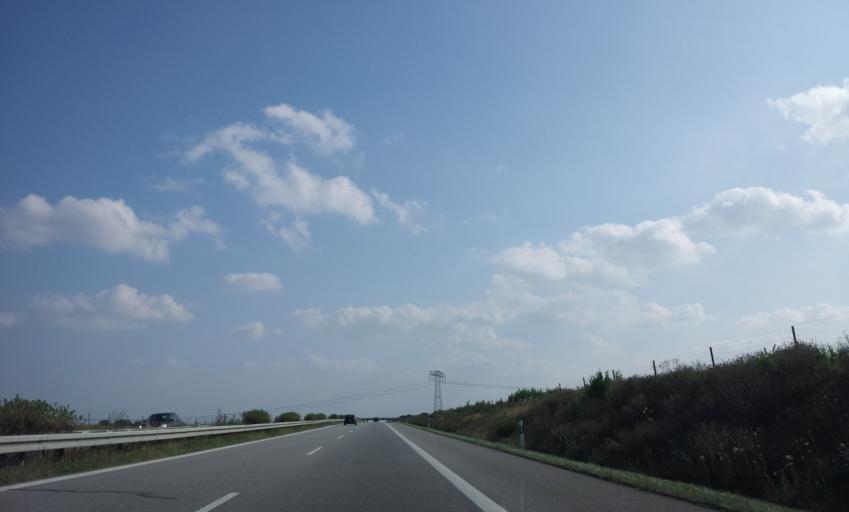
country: DE
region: Mecklenburg-Vorpommern
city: Burow
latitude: 53.8206
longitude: 13.3240
